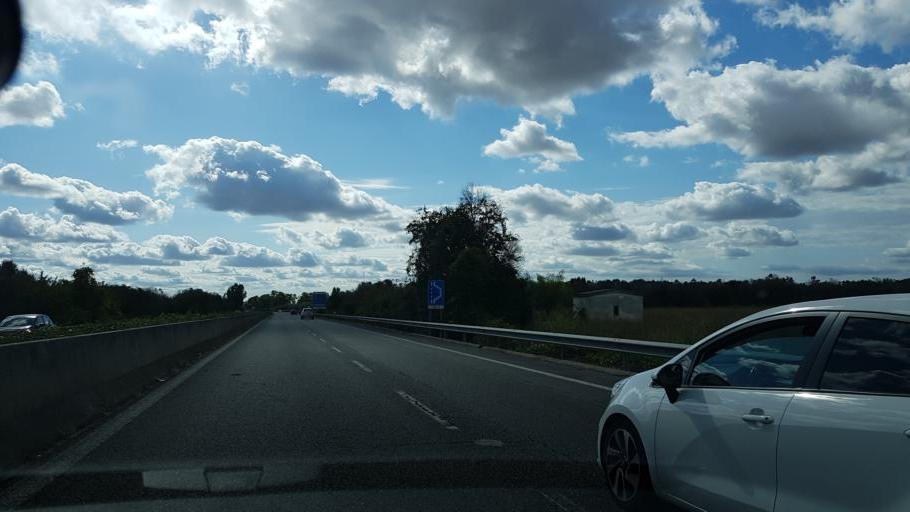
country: IT
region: Apulia
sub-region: Provincia di Brindisi
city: San Pietro Vernotico
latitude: 40.5278
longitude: 18.0122
